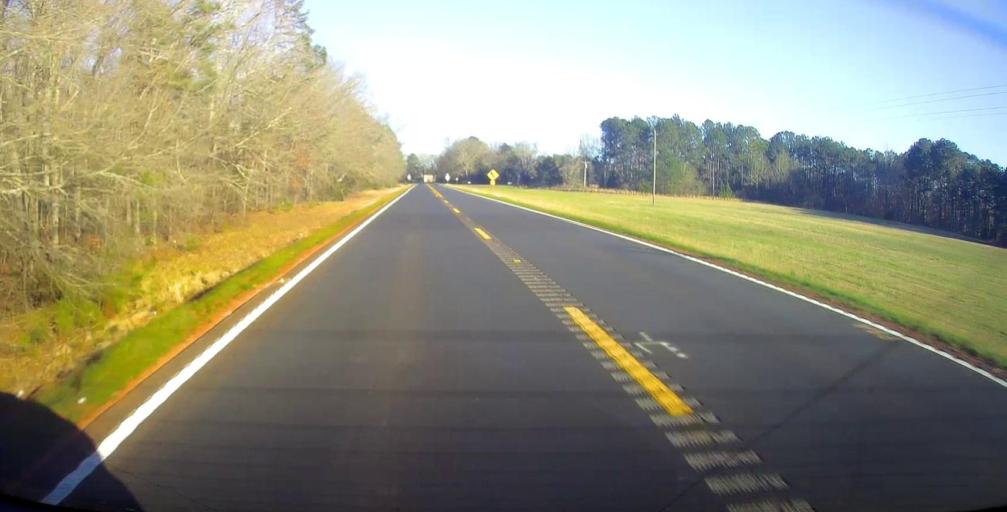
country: US
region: Georgia
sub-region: Meriwether County
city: Greenville
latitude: 32.9123
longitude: -84.7415
